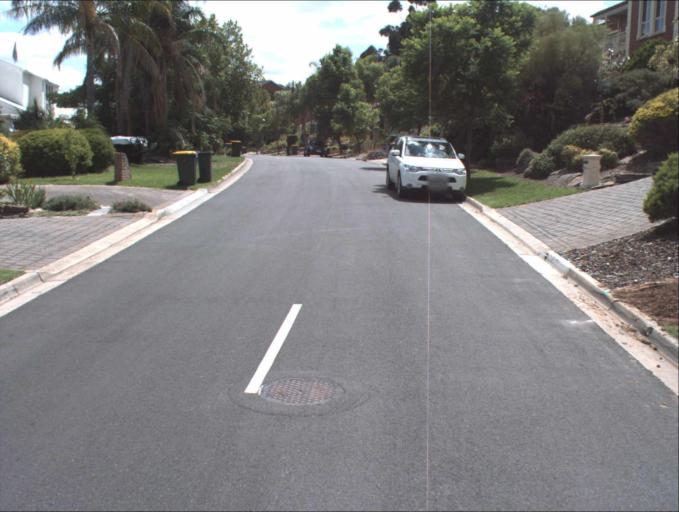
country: AU
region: South Australia
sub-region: Campbelltown
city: Paradise
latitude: -34.8668
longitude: 138.6680
